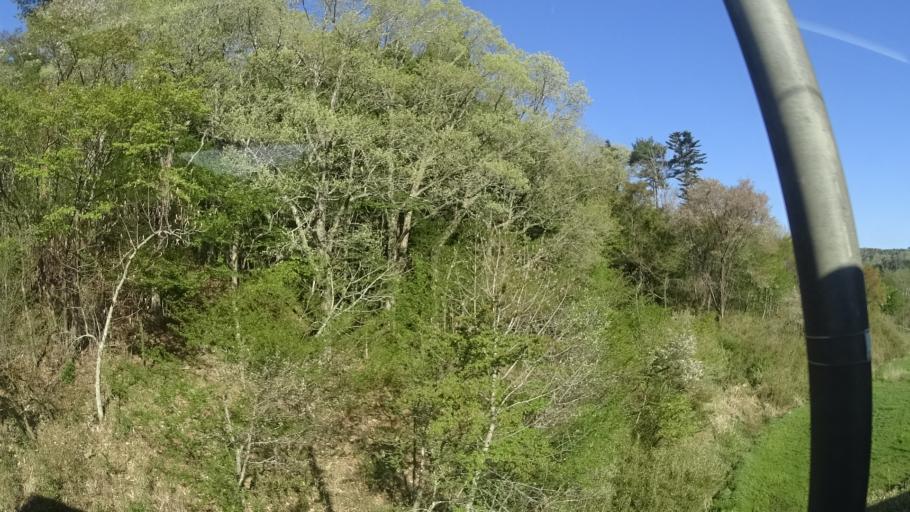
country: JP
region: Fukushima
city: Namie
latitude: 37.5234
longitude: 140.9770
